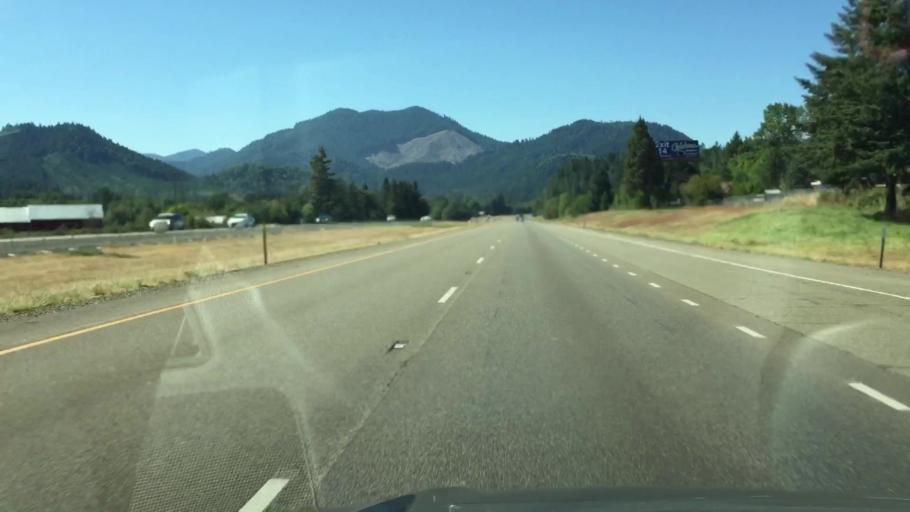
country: US
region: Oregon
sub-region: Douglas County
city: Canyonville
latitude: 42.7958
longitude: -123.2572
